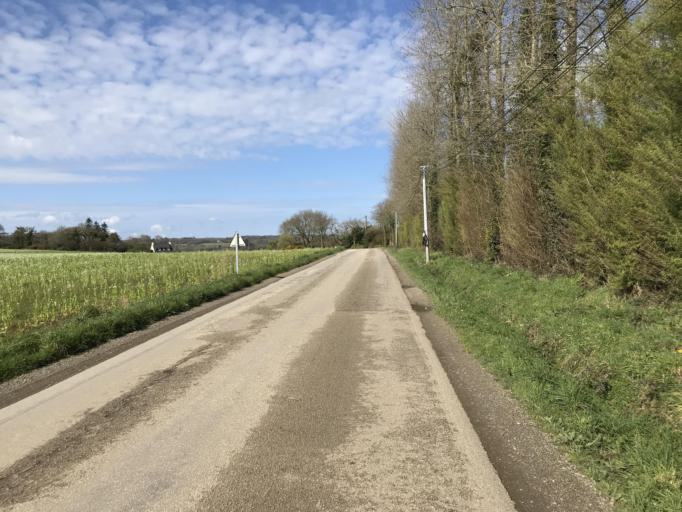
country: FR
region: Brittany
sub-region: Departement du Finistere
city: Loperhet
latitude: 48.3729
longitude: -4.2844
